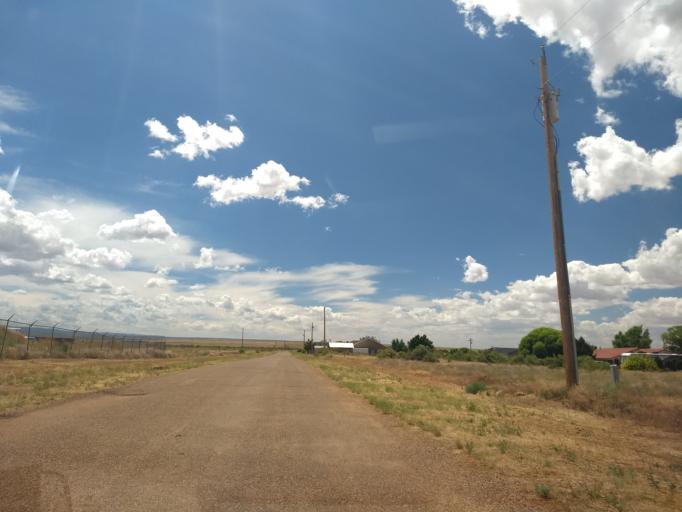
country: US
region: Arizona
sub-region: Coconino County
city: Fredonia
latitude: 36.9437
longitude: -112.5179
